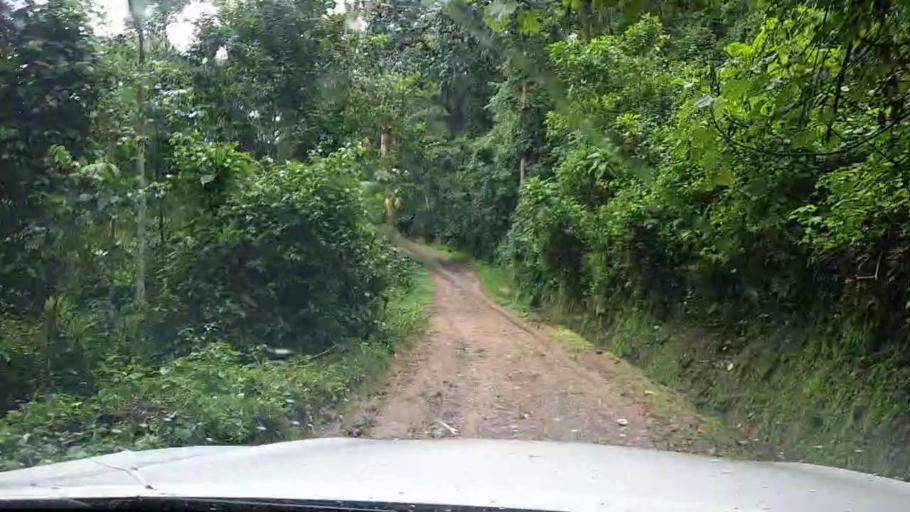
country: RW
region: Western Province
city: Cyangugu
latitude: -2.5589
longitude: 28.9864
